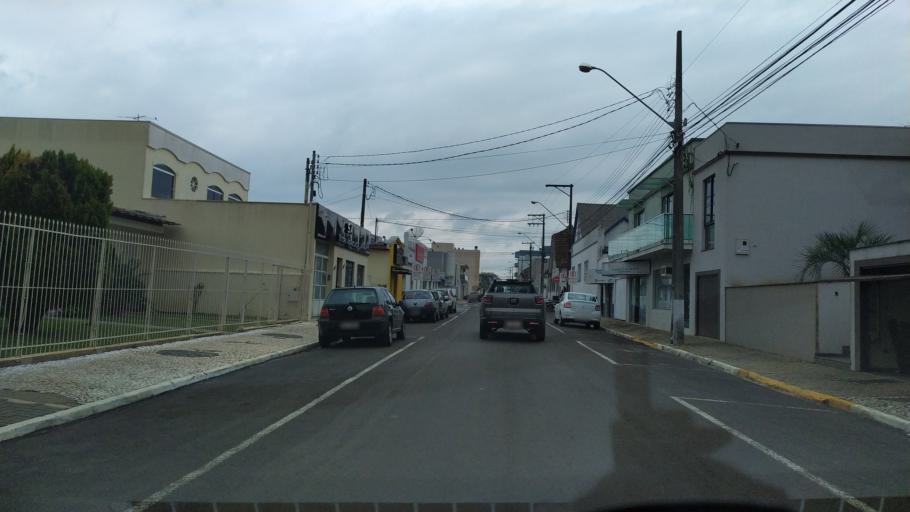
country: BR
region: Parana
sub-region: Palmas
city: Palmas
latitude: -26.4843
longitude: -51.9897
